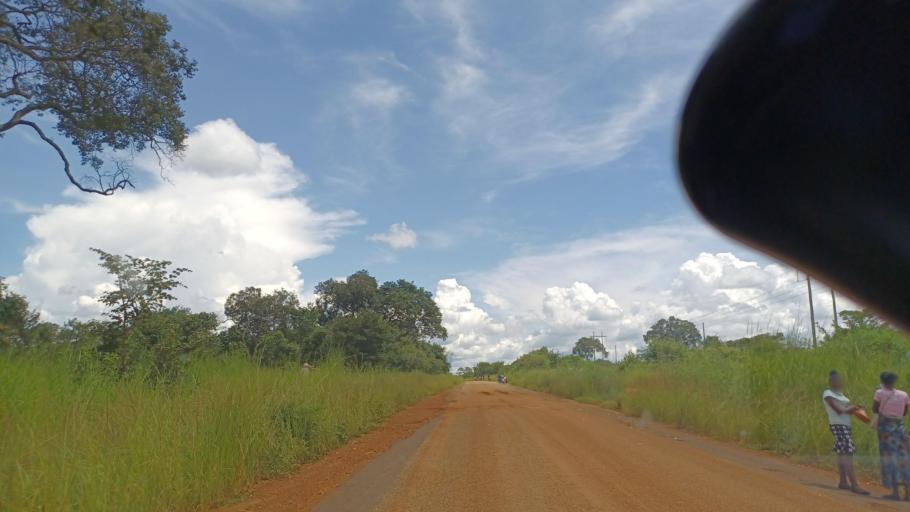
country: ZM
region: North-Western
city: Solwezi
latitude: -12.5578
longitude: 26.1435
